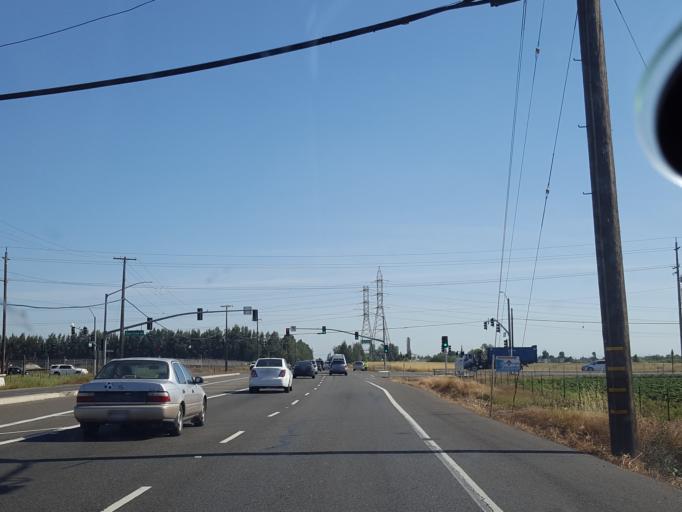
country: US
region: California
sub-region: Sacramento County
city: Vineyard
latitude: 38.5121
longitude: -121.3351
